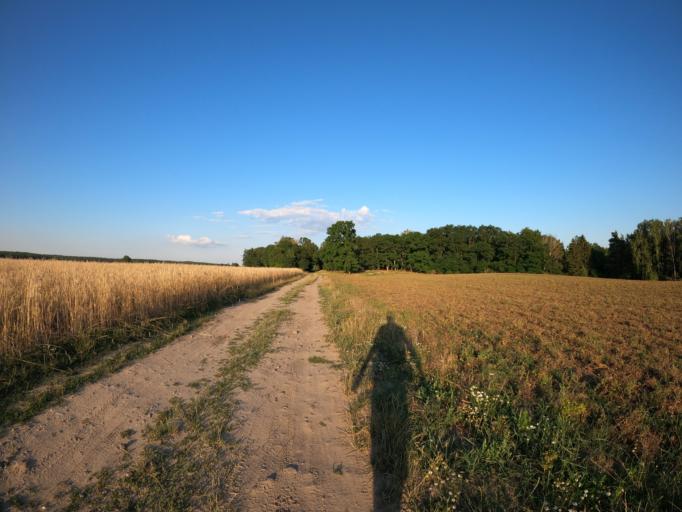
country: DE
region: Brandenburg
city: Althuttendorf
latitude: 53.0264
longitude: 13.8705
